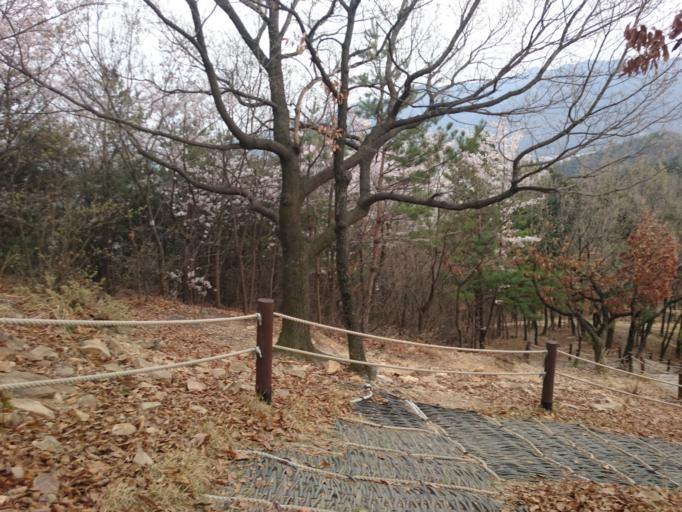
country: KR
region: Daegu
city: Daegu
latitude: 35.8463
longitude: 128.5563
